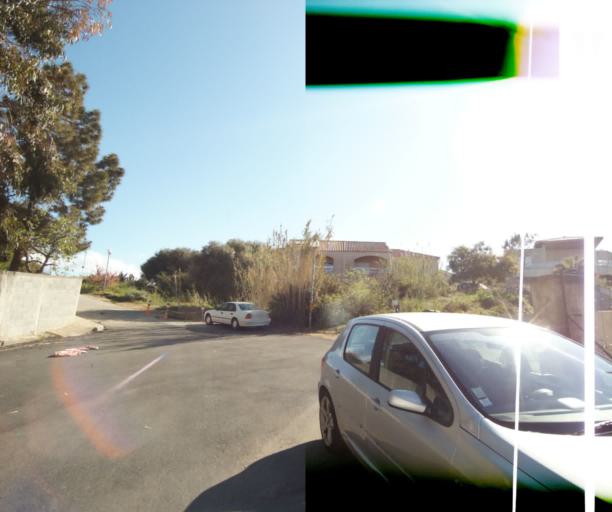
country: FR
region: Corsica
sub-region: Departement de la Corse-du-Sud
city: Propriano
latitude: 41.6682
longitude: 8.8996
